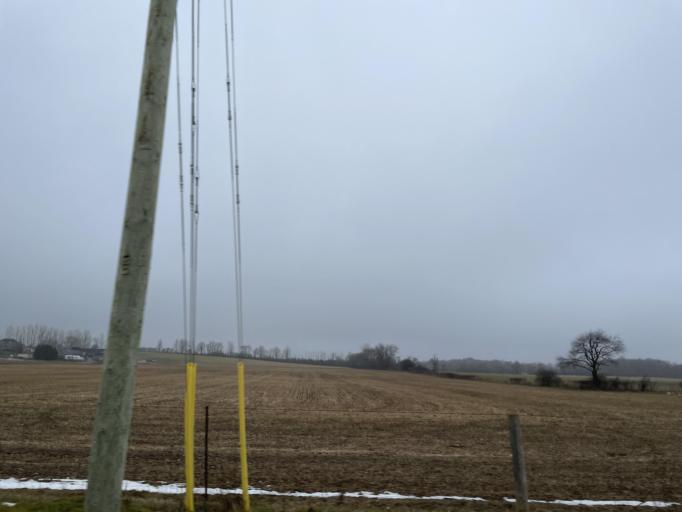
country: CA
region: Ontario
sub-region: Wellington County
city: Guelph
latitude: 43.4846
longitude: -80.3388
